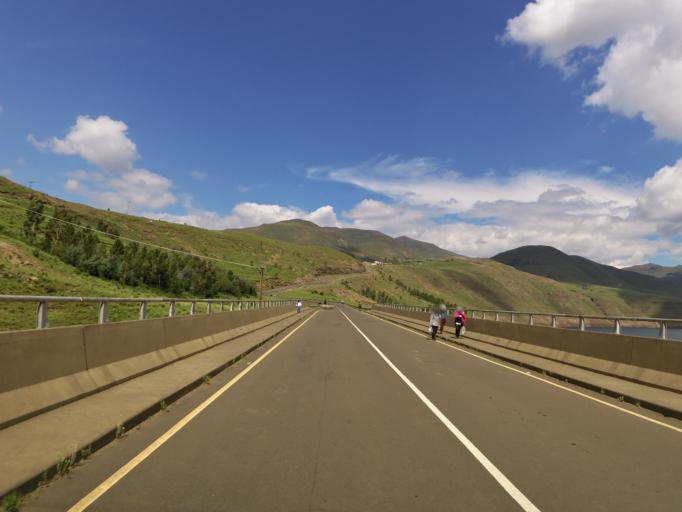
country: LS
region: Thaba-Tseka
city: Thaba-Tseka
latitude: -29.1825
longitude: 28.4834
